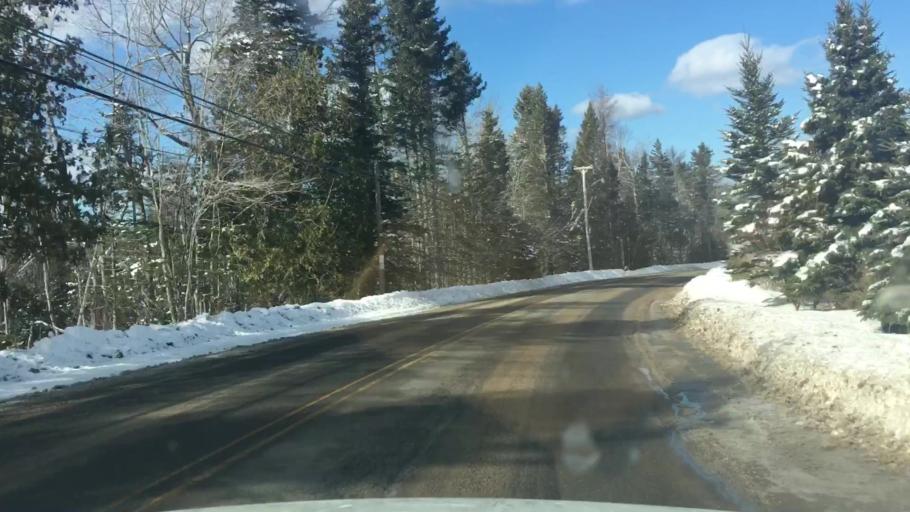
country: US
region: Maine
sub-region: Washington County
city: Machias
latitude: 44.6930
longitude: -67.4672
